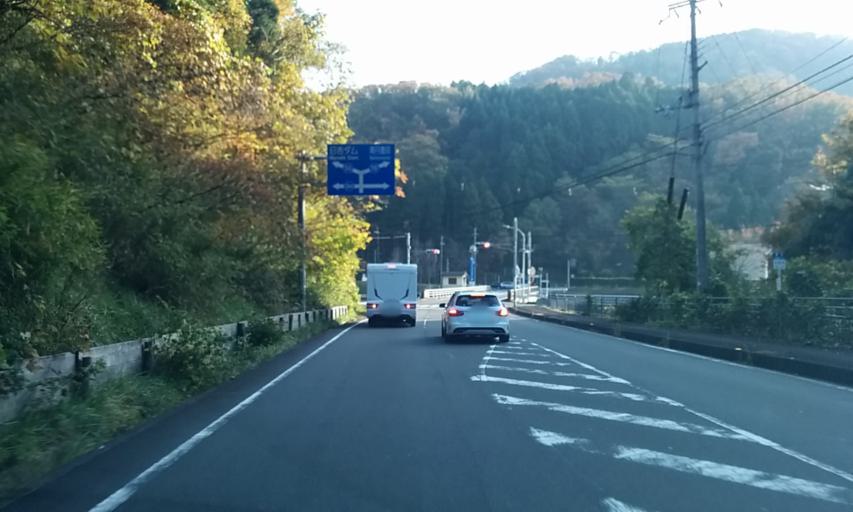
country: JP
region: Kyoto
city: Kameoka
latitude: 35.1550
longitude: 135.5135
